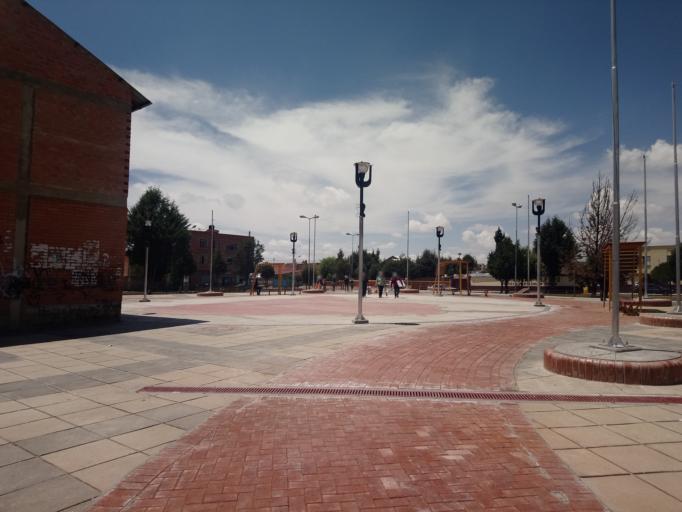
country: BO
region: La Paz
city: La Paz
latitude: -16.5448
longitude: -68.1899
